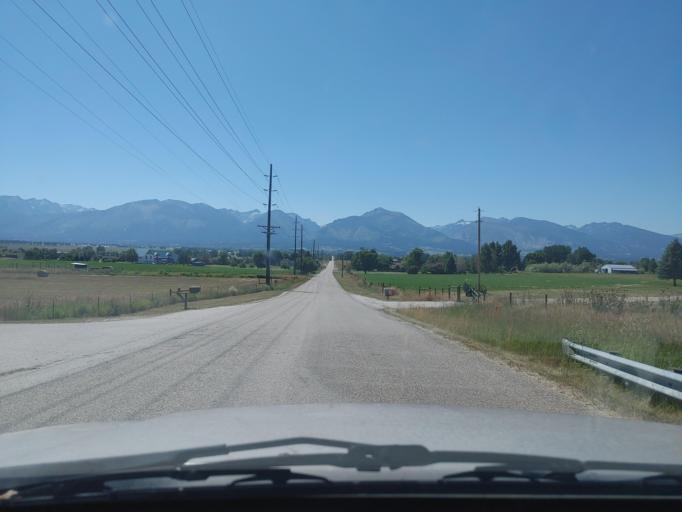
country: US
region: Montana
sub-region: Ravalli County
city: Hamilton
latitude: 46.2768
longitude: -114.0551
